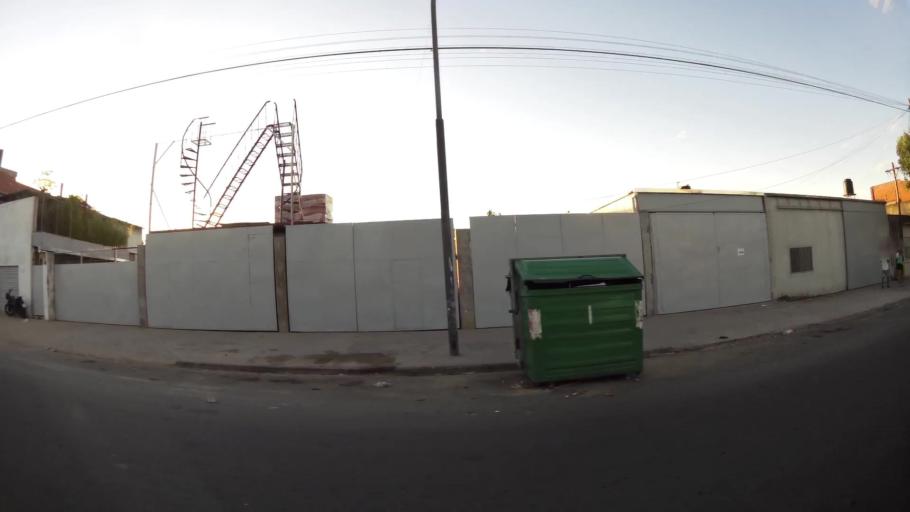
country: AR
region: Santa Fe
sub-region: Departamento de Rosario
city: Rosario
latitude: -32.9702
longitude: -60.6870
